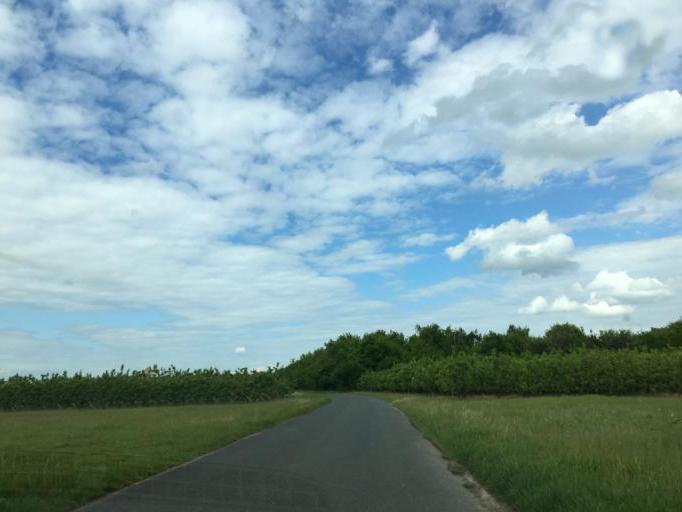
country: FR
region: Centre
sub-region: Departement du Loiret
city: Mareau-aux-Pres
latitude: 47.8350
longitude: 1.8029
